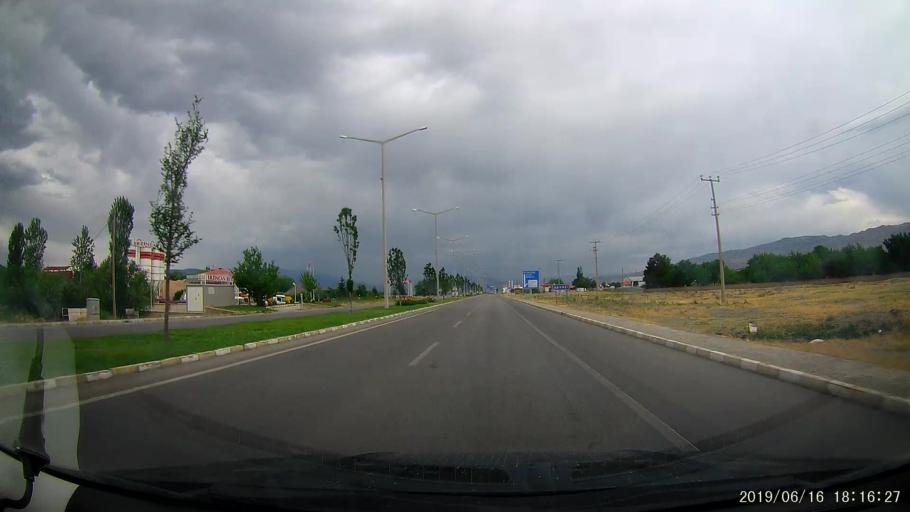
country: TR
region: Erzincan
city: Erzincan
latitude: 39.7284
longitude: 39.5479
